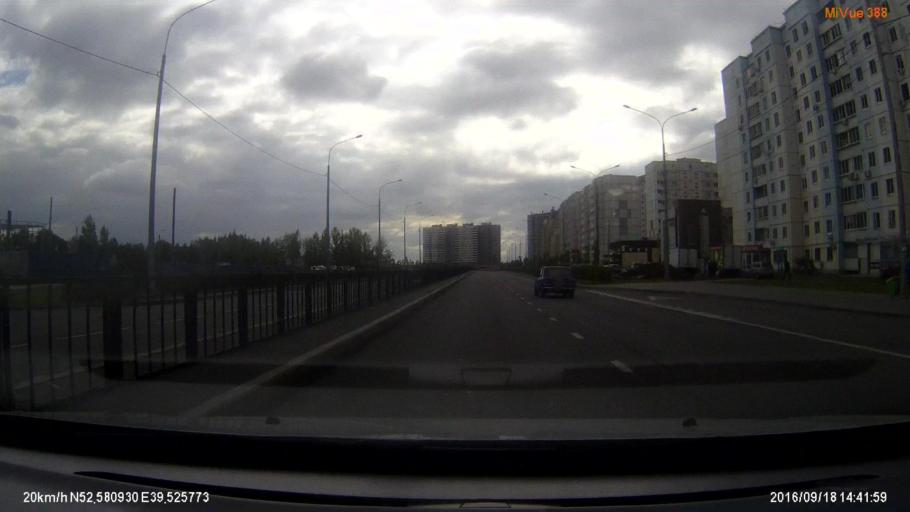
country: RU
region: Lipetsk
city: Syrskoye
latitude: 52.5809
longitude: 39.5257
